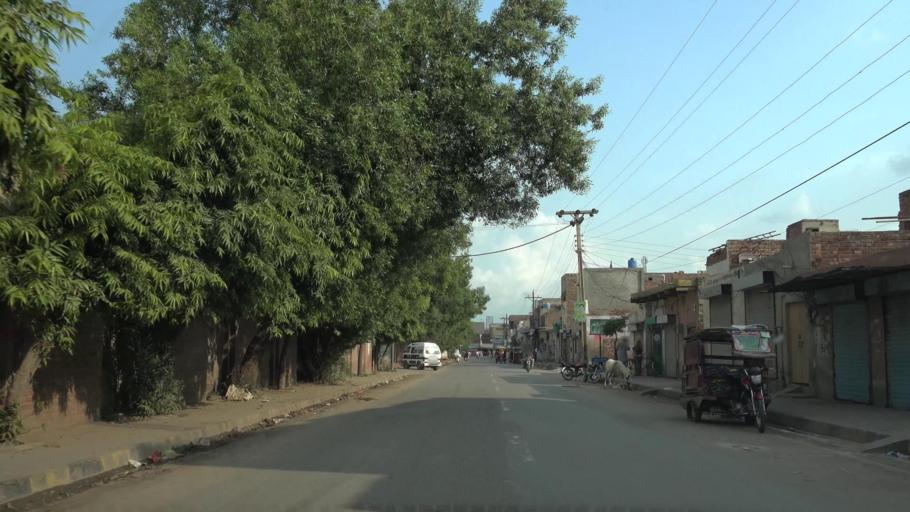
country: PK
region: Punjab
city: Nankana Sahib
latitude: 31.4499
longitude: 73.6986
